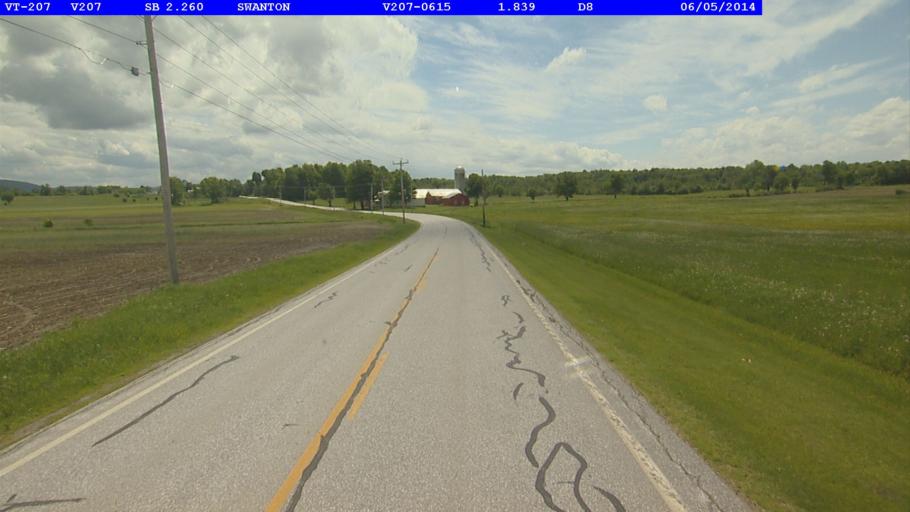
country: US
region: Vermont
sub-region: Franklin County
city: Saint Albans
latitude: 44.8716
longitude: -73.0750
